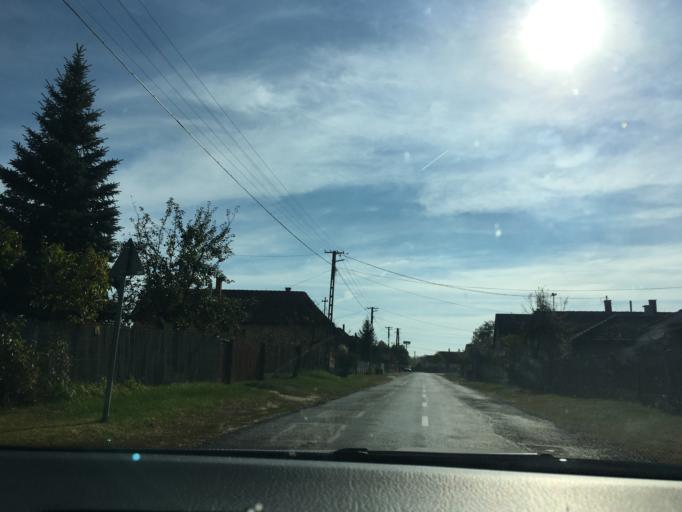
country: HU
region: Hajdu-Bihar
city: Nyirabrany
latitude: 47.5343
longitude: 22.0002
